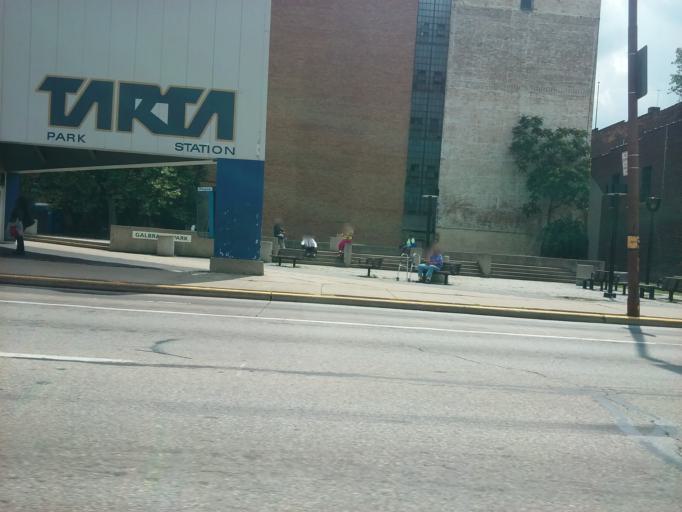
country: US
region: Ohio
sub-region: Lucas County
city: Toledo
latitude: 41.6525
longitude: -83.5379
